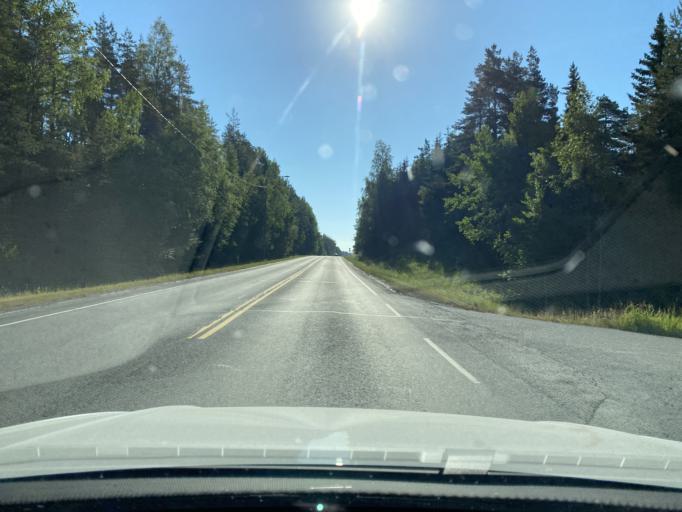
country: FI
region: Haeme
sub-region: Forssa
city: Forssa
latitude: 60.8292
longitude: 23.6633
